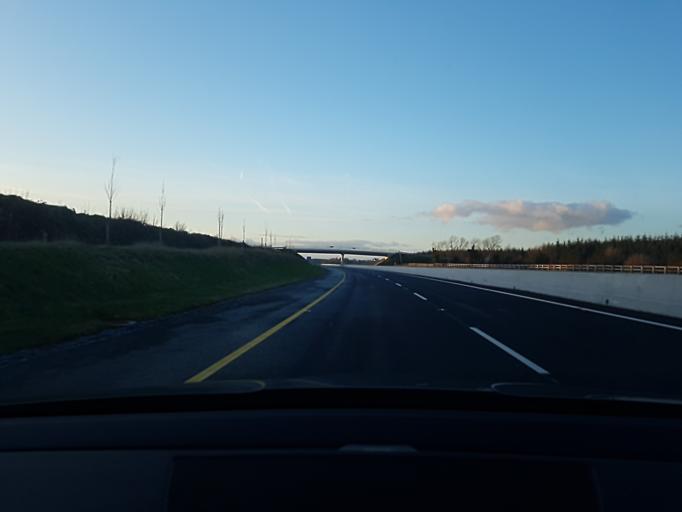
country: IE
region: Connaught
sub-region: County Galway
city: Tuam
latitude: 53.4896
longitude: -8.8673
